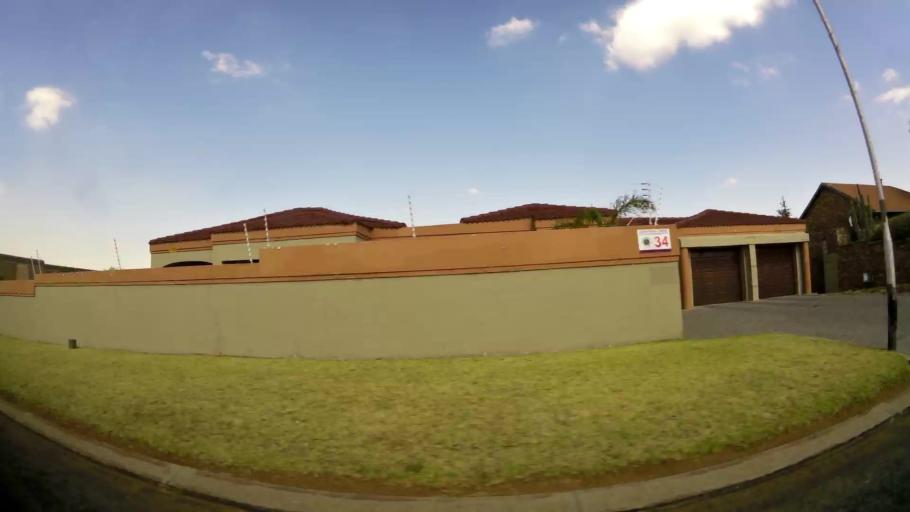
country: ZA
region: Gauteng
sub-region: West Rand District Municipality
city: Randfontein
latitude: -26.1675
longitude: 27.7509
